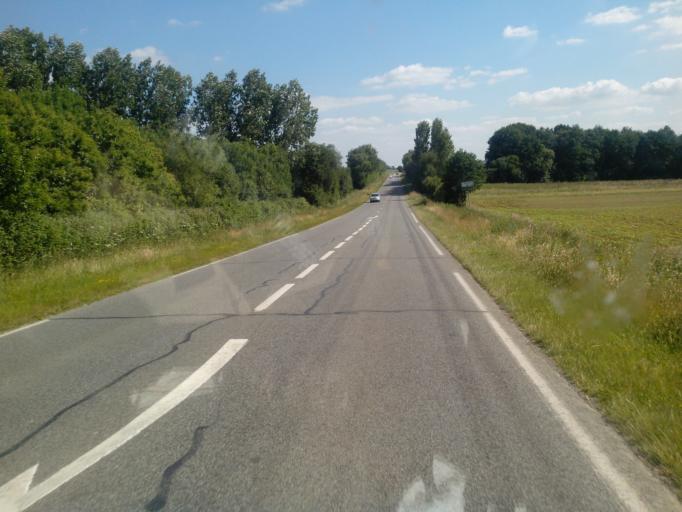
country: FR
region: Brittany
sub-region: Departement d'Ille-et-Vilaine
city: Acigne
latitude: 48.1445
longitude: -1.5166
